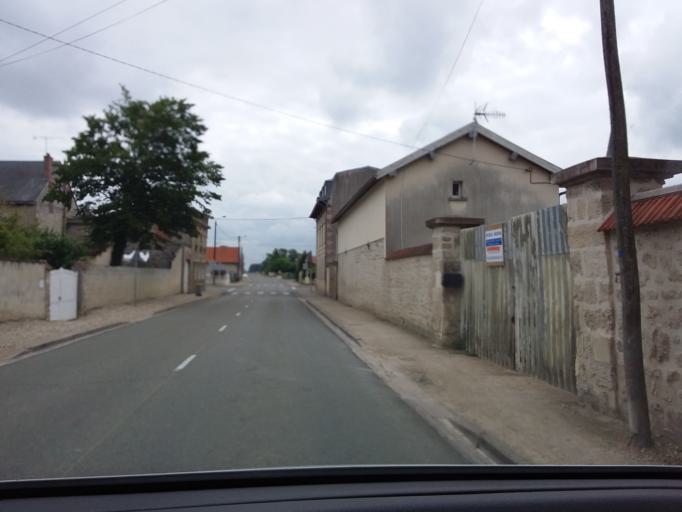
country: FR
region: Champagne-Ardenne
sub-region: Departement de la Marne
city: Cormicy
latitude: 49.4077
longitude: 3.8202
